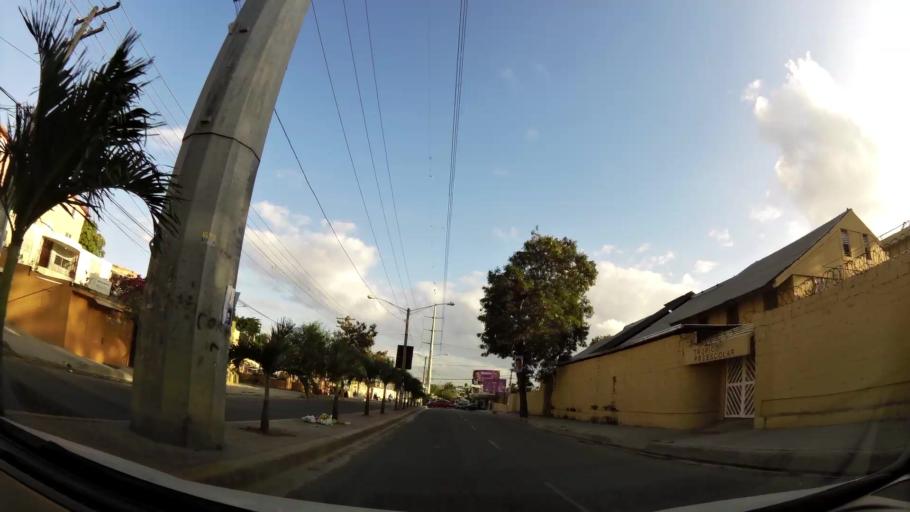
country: DO
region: Nacional
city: La Agustina
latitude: 18.5407
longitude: -69.9281
